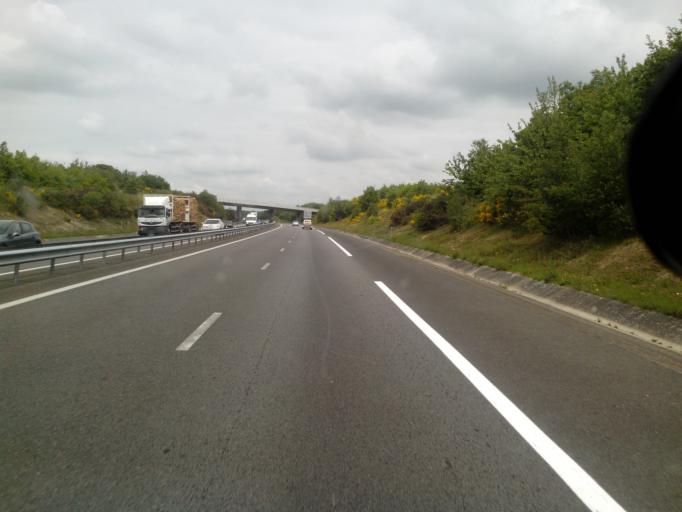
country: FR
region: Brittany
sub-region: Departement d'Ille-et-Vilaine
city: Saint-Aubin-du-Cormier
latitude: 48.2518
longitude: -1.4263
